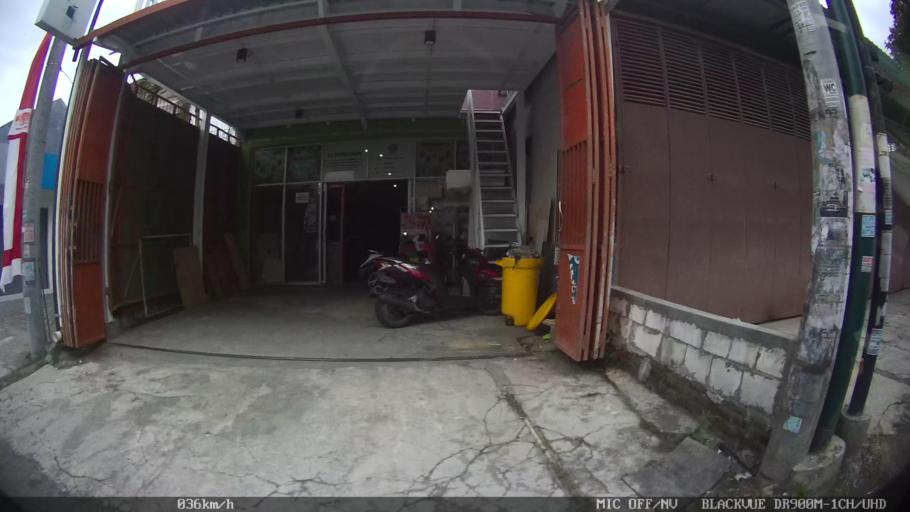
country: ID
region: Daerah Istimewa Yogyakarta
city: Depok
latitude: -7.8146
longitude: 110.4171
